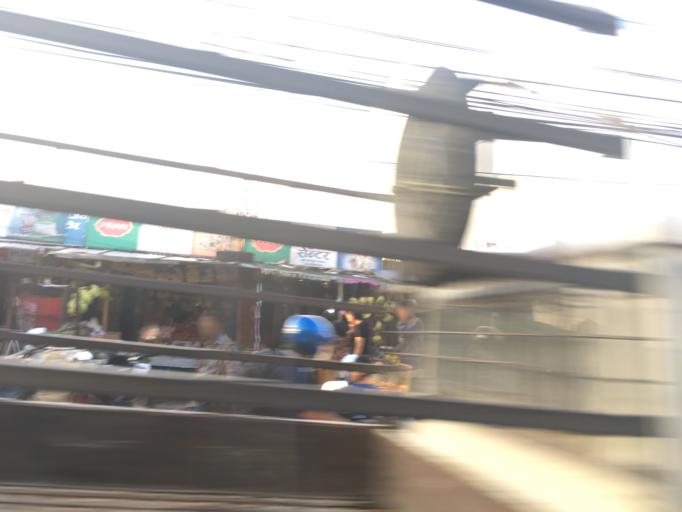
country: NP
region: Central Region
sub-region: Bagmati Zone
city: Bhaktapur
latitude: 27.6775
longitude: 85.4372
